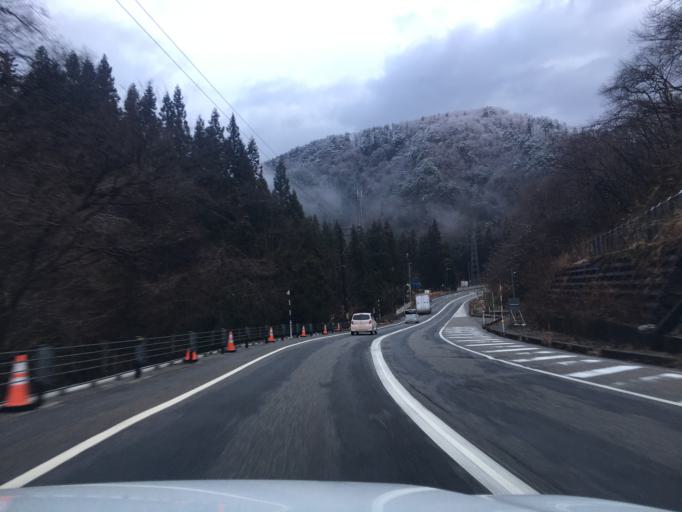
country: JP
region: Niigata
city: Murakami
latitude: 38.4203
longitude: 139.5673
